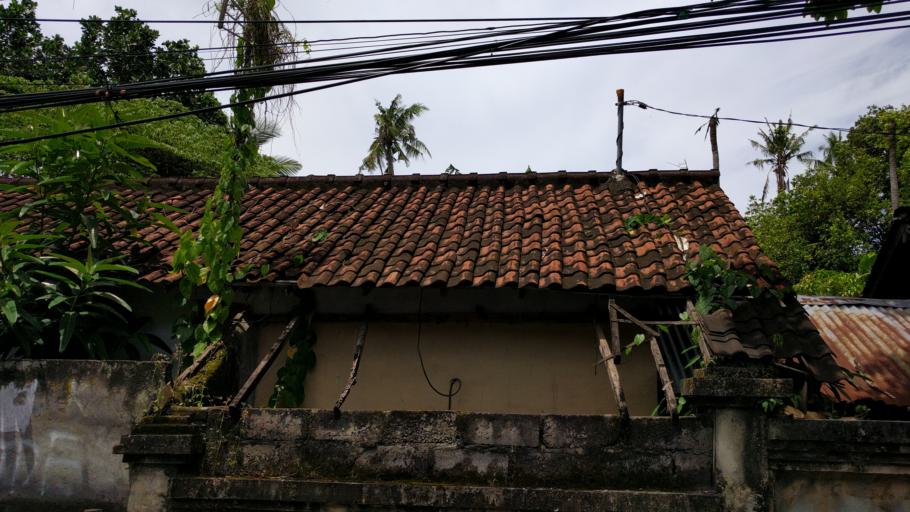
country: ID
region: Bali
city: Banjar Gunungpande
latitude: -8.6713
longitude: 115.1467
